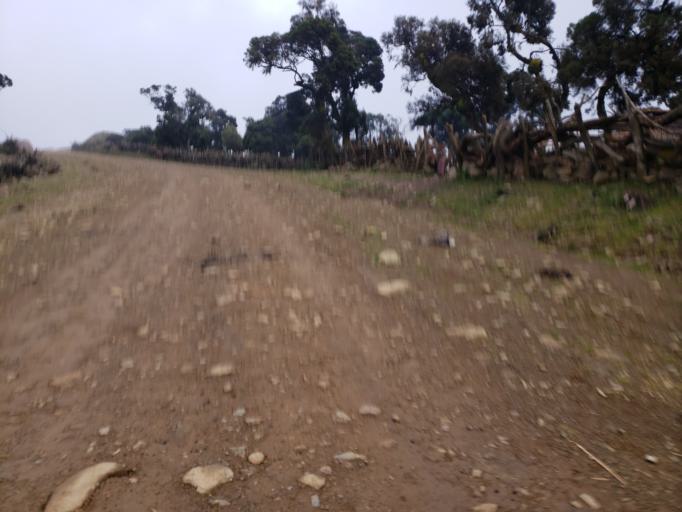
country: ET
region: Oromiya
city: Dodola
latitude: 6.7258
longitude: 39.4265
